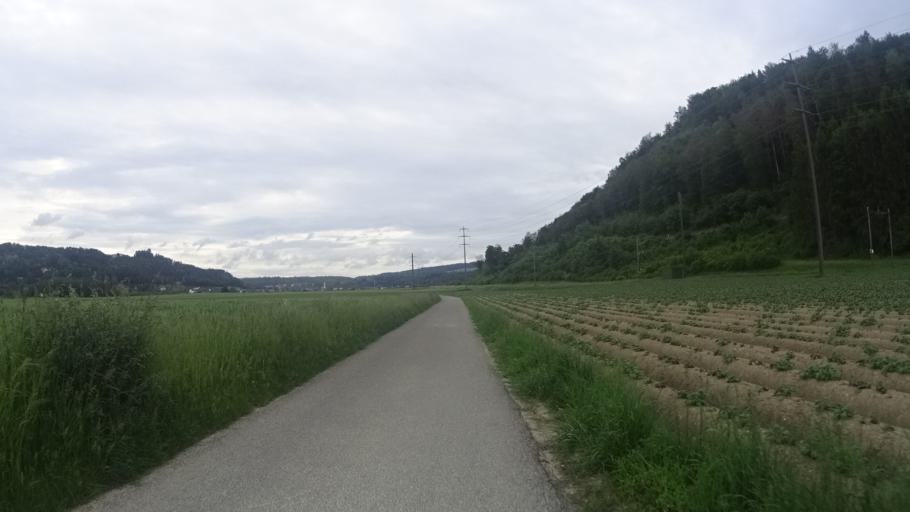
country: DE
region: Baden-Wuerttemberg
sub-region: Freiburg Region
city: Waldshut-Tiengen
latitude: 47.6124
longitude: 8.2086
